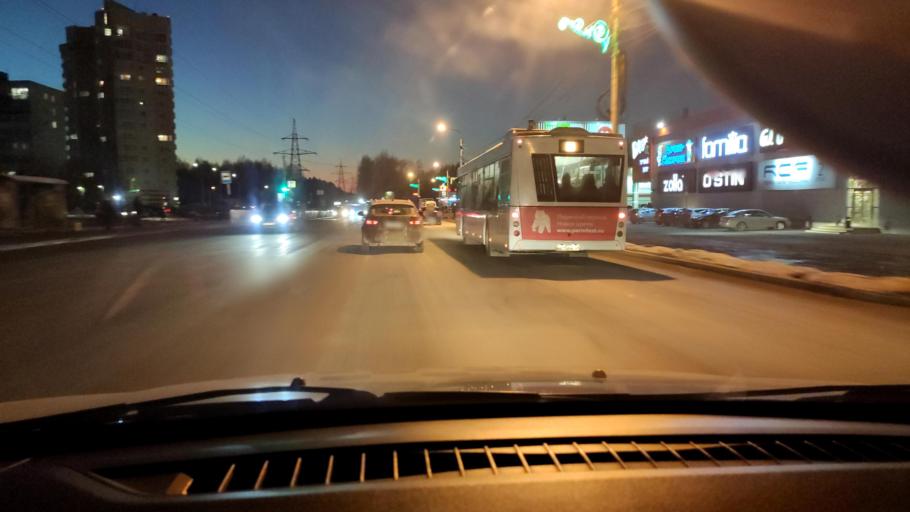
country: RU
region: Perm
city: Kondratovo
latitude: 58.0393
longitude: 56.0284
